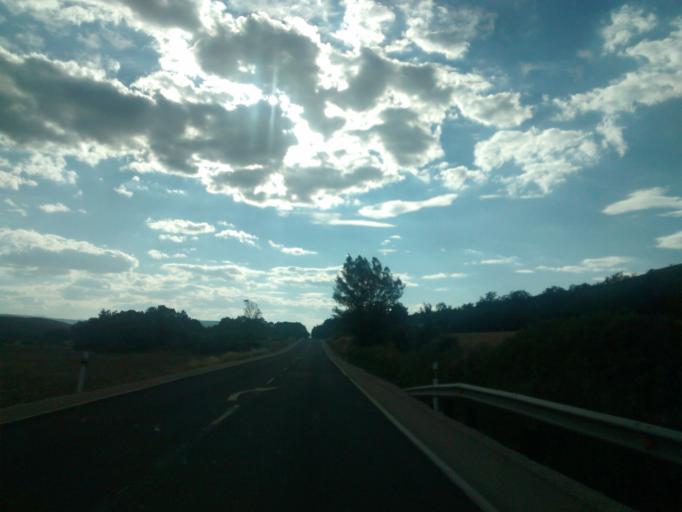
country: ES
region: Castille and Leon
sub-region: Provincia de Burgos
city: Basconcillos del Tozo
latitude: 42.6818
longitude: -3.9514
